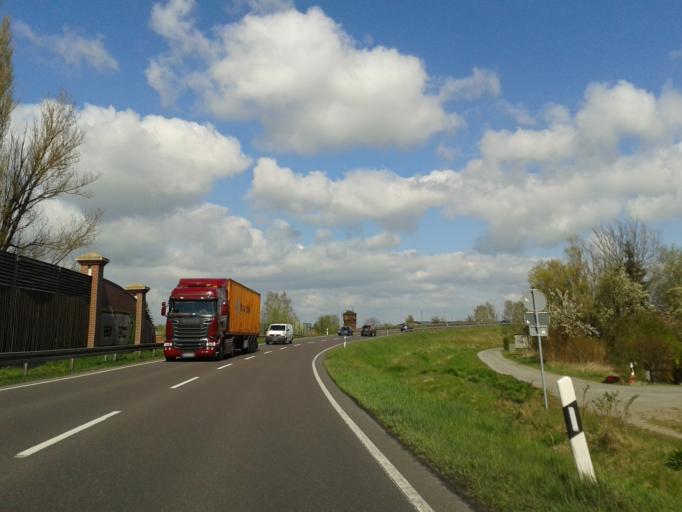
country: DE
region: Saxony-Anhalt
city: Salzwedel
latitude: 52.8549
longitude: 11.1657
